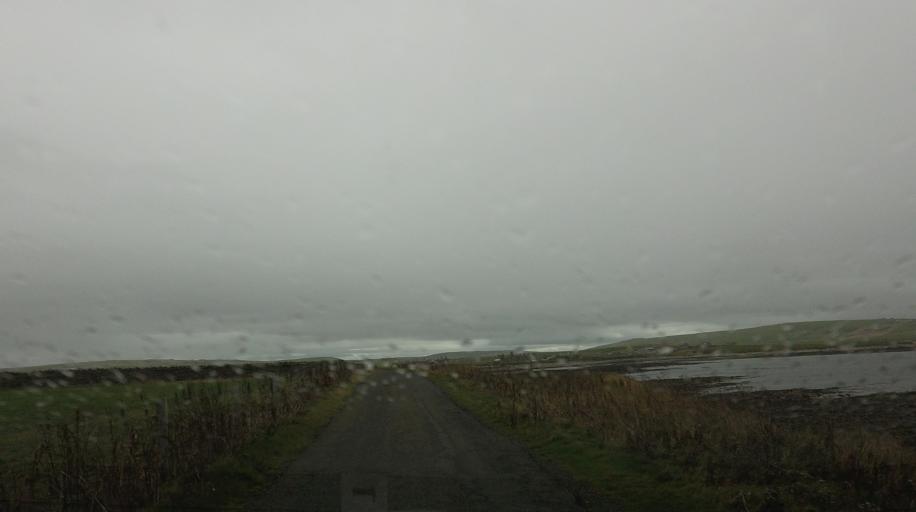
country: GB
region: Scotland
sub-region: Orkney Islands
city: Stromness
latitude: 59.1338
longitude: -3.3226
